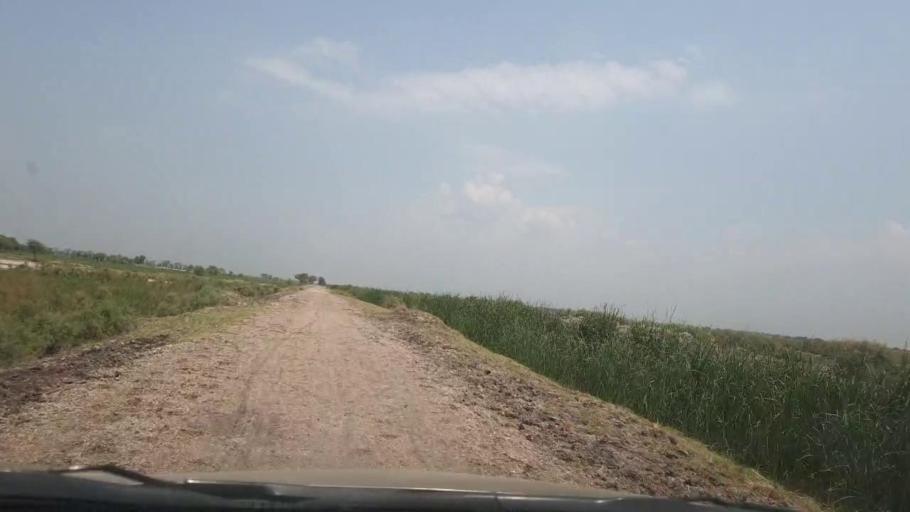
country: PK
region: Sindh
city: Naudero
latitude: 27.7191
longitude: 68.2999
